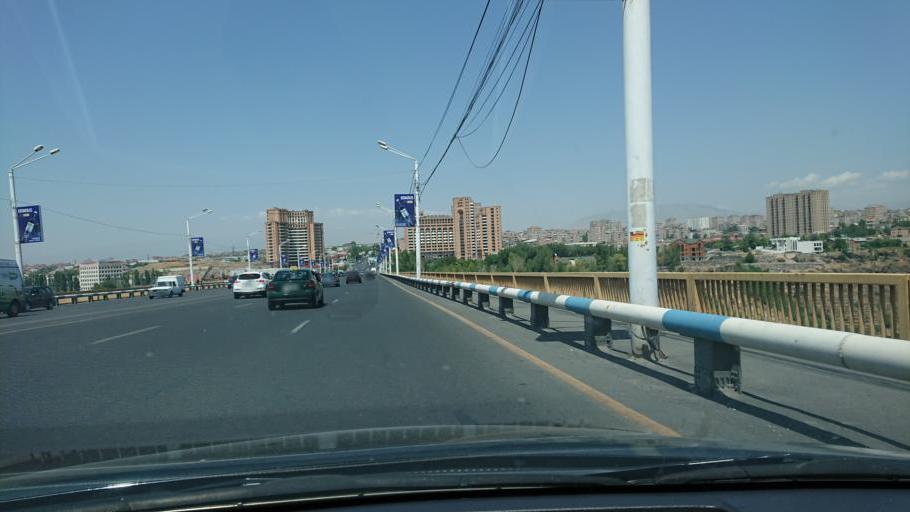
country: AM
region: Yerevan
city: Yerevan
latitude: 40.2088
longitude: 44.4943
